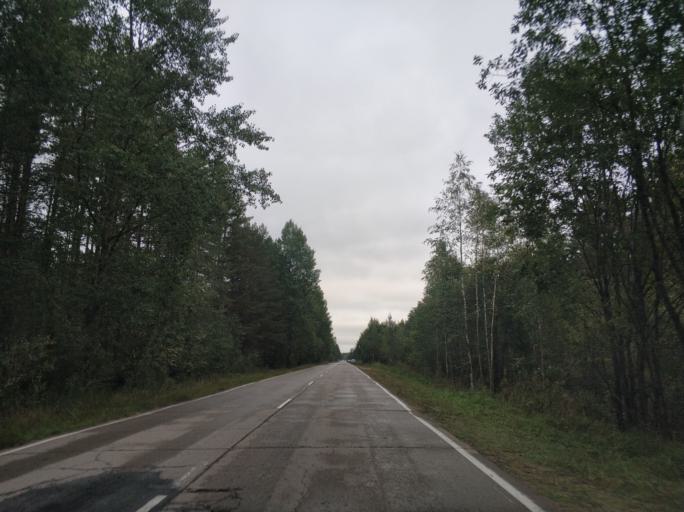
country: RU
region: Leningrad
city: Borisova Griva
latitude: 60.1744
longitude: 30.9194
